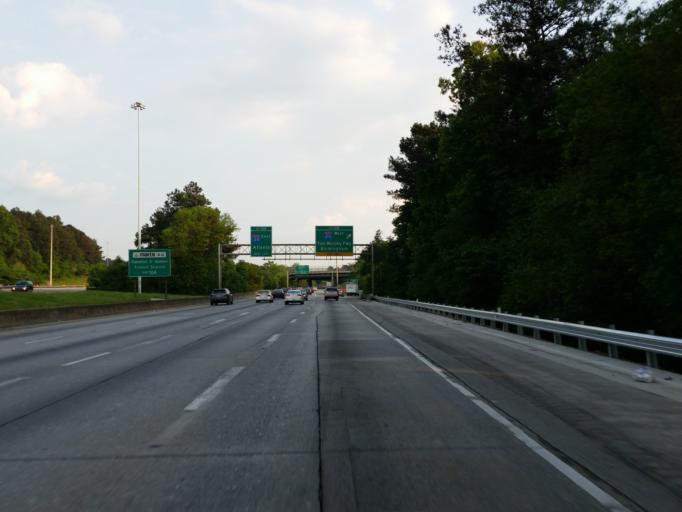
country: US
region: Georgia
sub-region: Cobb County
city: Mableton
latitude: 33.7692
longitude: -84.4953
